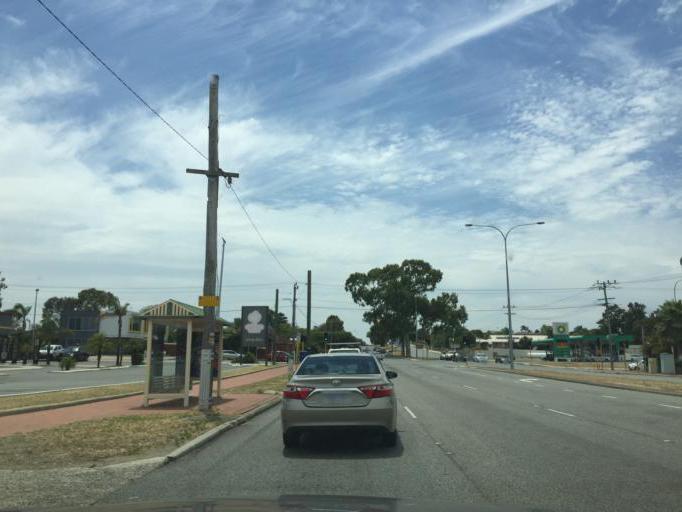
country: AU
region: Western Australia
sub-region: Melville
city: Kardinya
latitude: -32.0685
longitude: 115.8186
